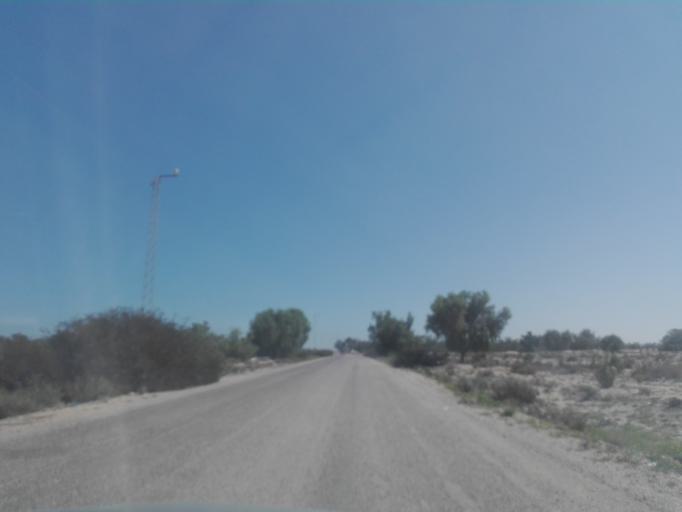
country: TN
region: Qabis
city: Gabes
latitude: 33.8723
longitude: 10.0344
